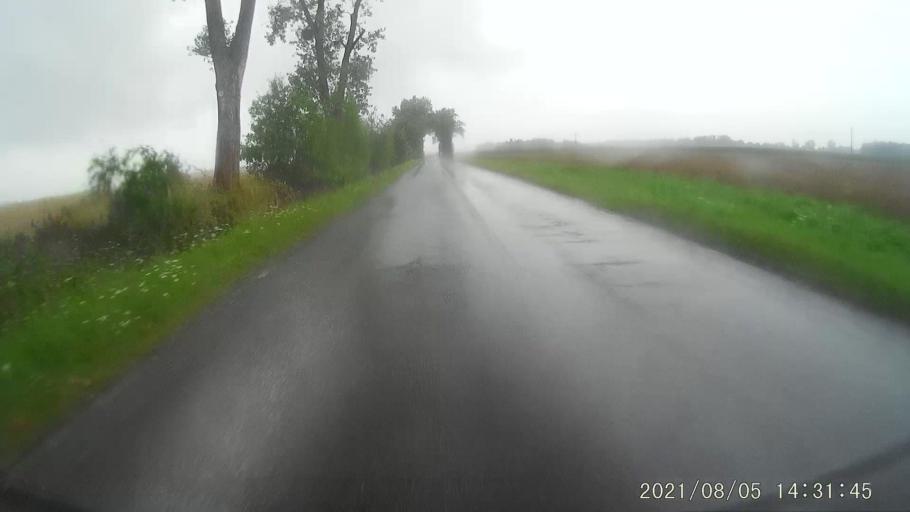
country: PL
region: Opole Voivodeship
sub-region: Powiat nyski
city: Korfantow
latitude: 50.4720
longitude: 17.5537
